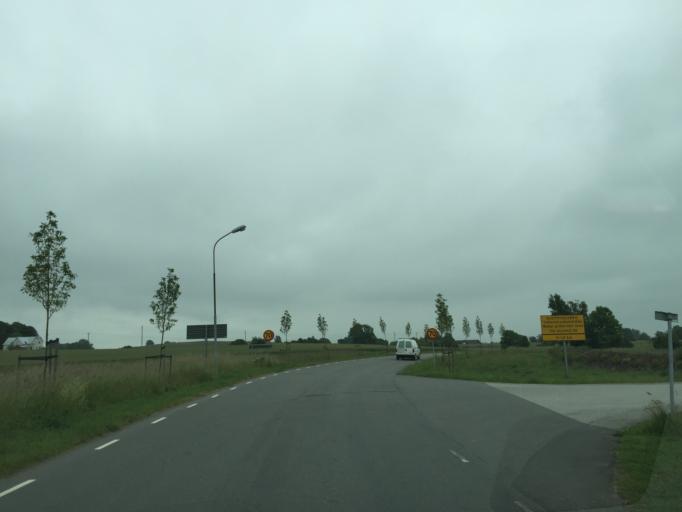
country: SE
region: Skane
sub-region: Ystads Kommun
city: Kopingebro
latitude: 55.4490
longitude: 14.0252
